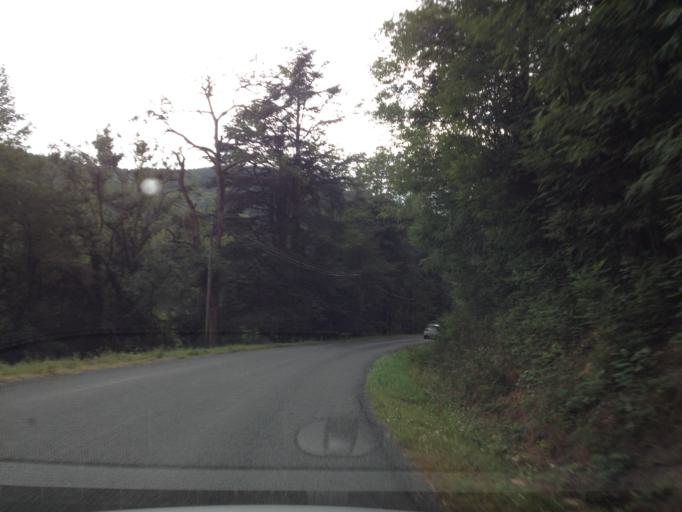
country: FR
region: Rhone-Alpes
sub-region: Departement de la Loire
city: Renaison
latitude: 46.0481
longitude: 3.9039
